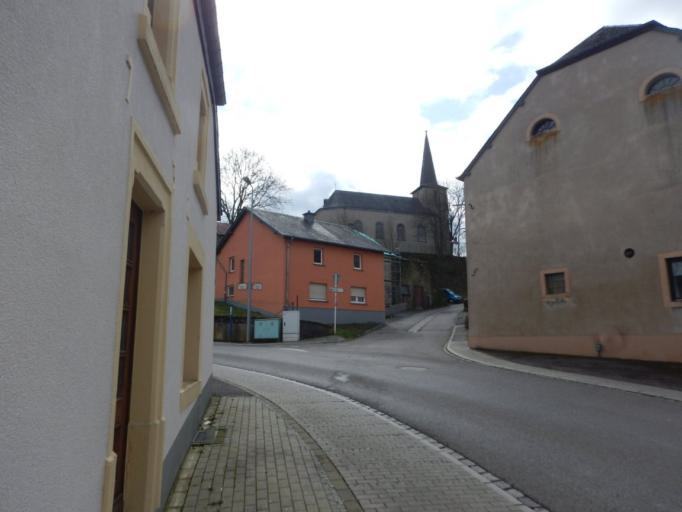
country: LU
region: Diekirch
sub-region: Canton de Wiltz
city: Esch-sur-Sure
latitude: 49.9216
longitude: 5.9018
